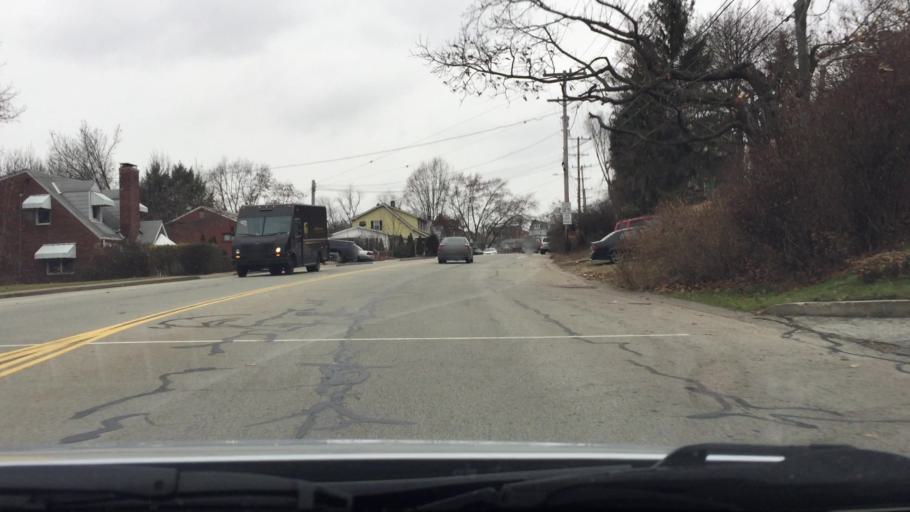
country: US
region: Pennsylvania
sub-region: Allegheny County
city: West View
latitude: 40.5182
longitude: -80.0368
